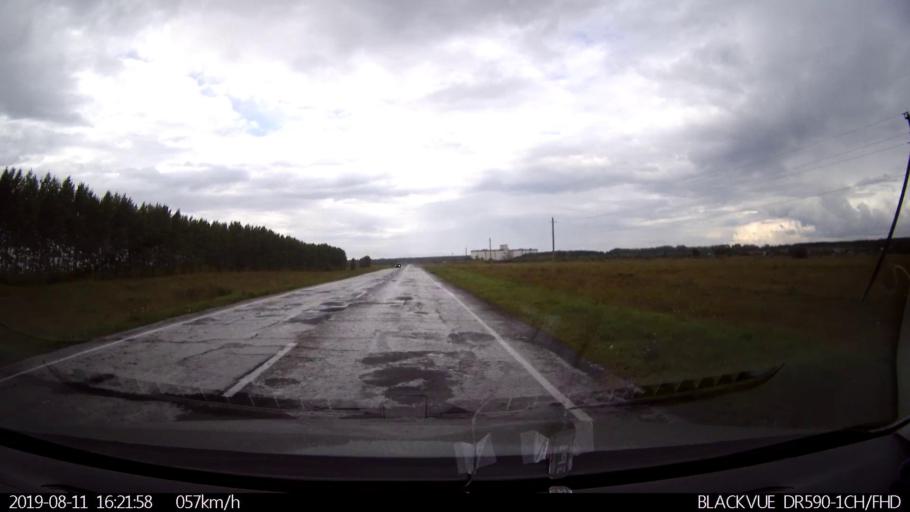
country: RU
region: Ulyanovsk
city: Mayna
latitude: 54.0840
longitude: 47.5954
